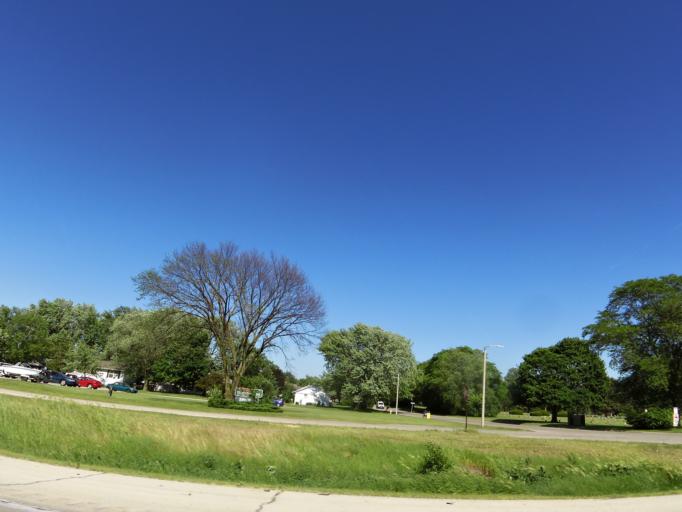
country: US
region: Illinois
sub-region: Winnebago County
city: South Beloit
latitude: 42.4858
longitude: -89.0195
